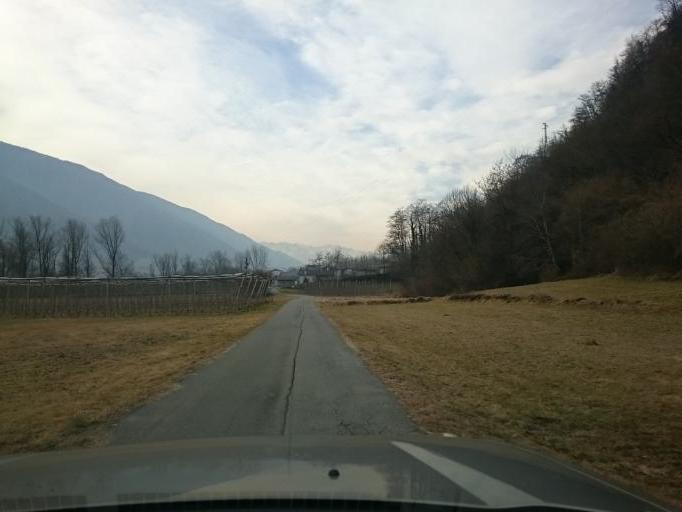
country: IT
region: Lombardy
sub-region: Provincia di Sondrio
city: Lovero
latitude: 46.2423
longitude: 10.2308
